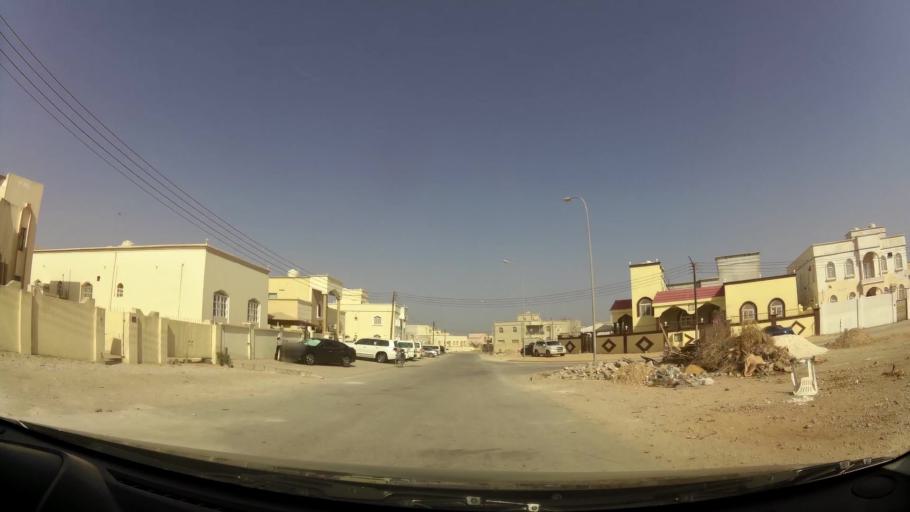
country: OM
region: Zufar
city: Salalah
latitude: 17.0144
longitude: 54.0103
